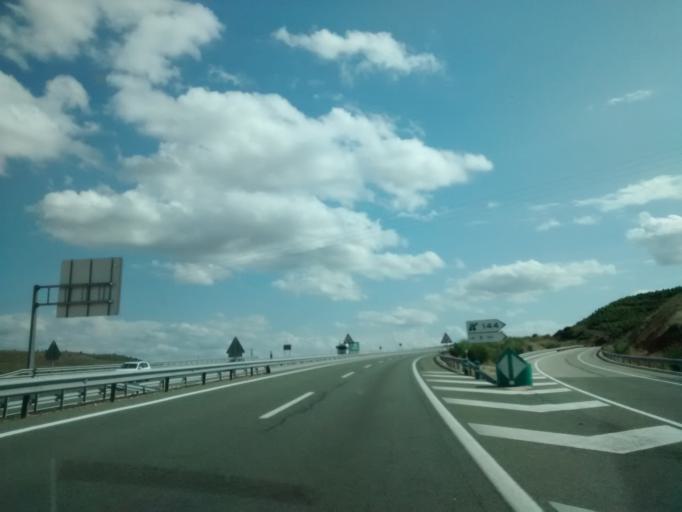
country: ES
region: Castille and Leon
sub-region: Provincia de Soria
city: Medinaceli
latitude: 41.1174
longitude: -2.4429
